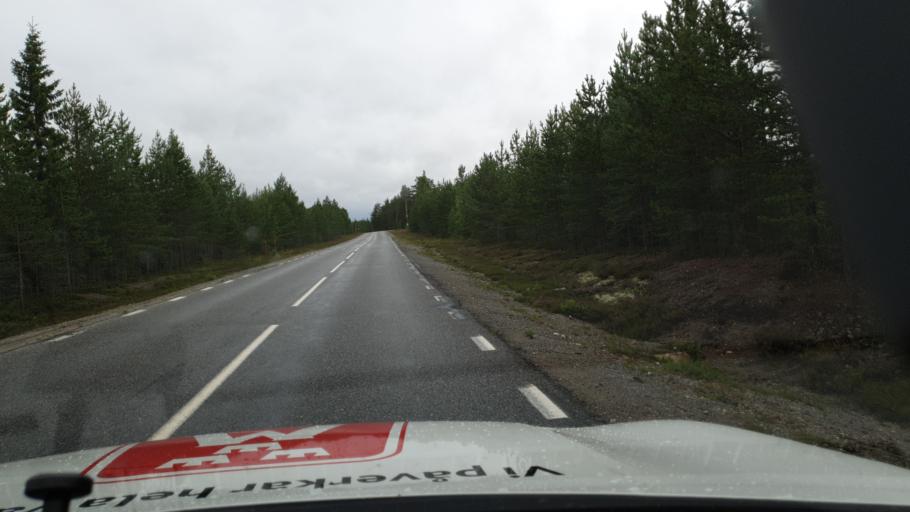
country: SE
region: Vaesterbotten
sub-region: Umea Kommun
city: Saevar
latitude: 63.9382
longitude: 20.5249
